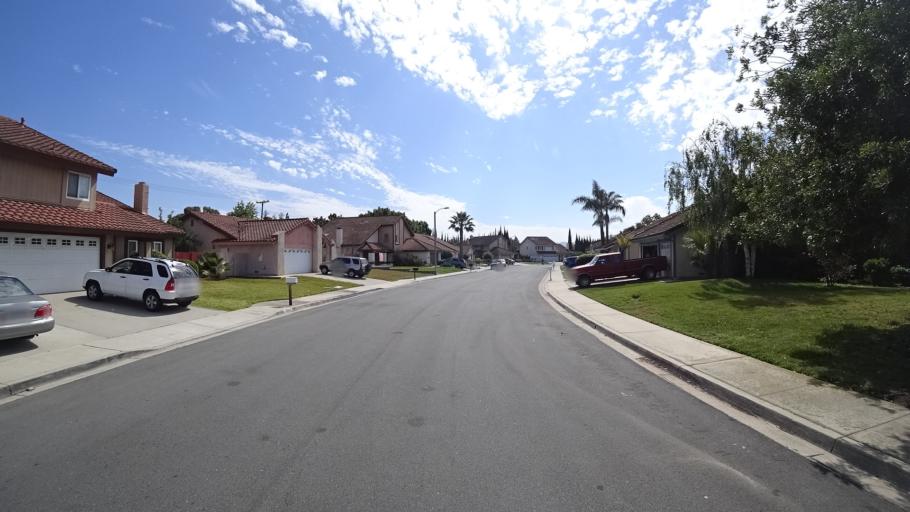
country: US
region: California
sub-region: Ventura County
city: Casa Conejo
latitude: 34.1879
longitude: -118.9373
